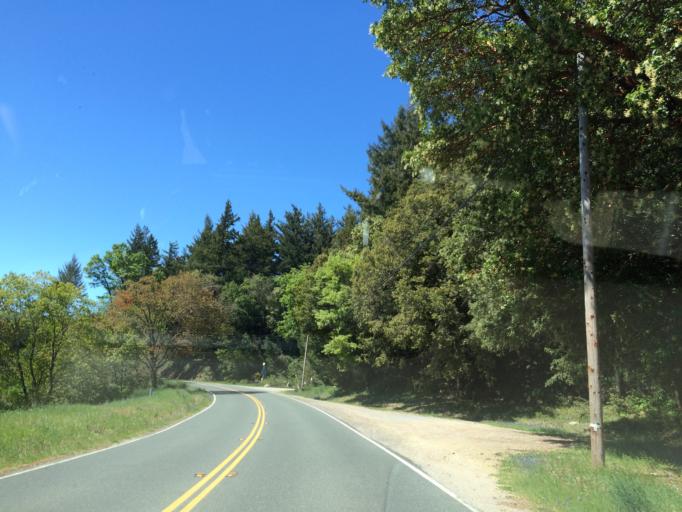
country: US
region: California
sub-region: Santa Clara County
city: Saratoga
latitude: 37.2187
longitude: -122.0730
